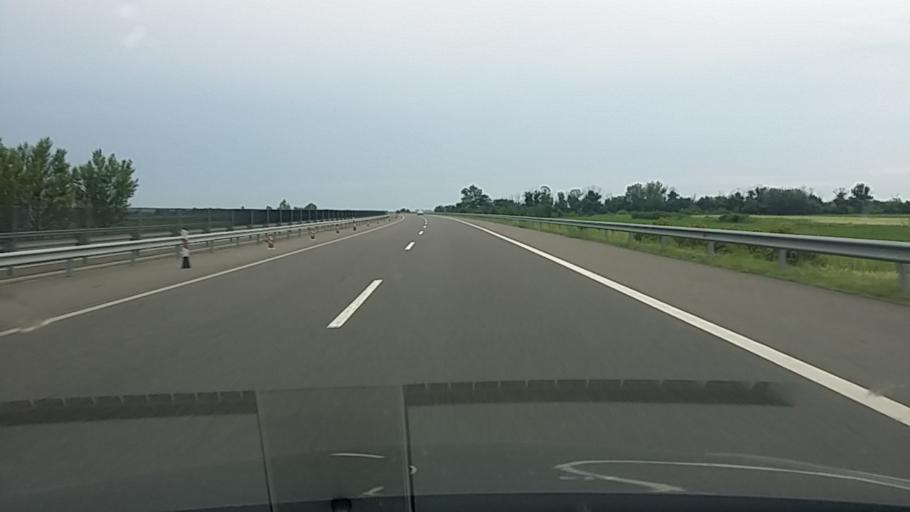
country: HU
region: Szabolcs-Szatmar-Bereg
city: Nagycserkesz
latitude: 47.9044
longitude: 21.5016
